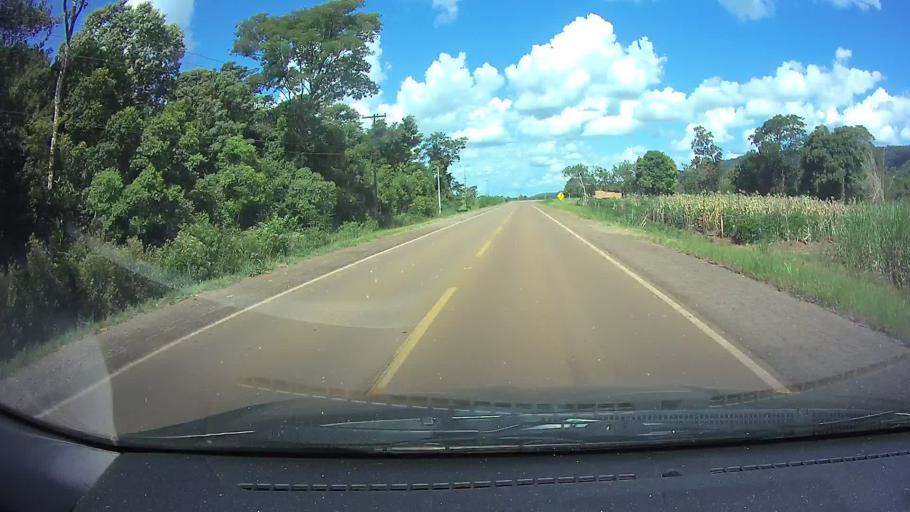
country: PY
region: Paraguari
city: La Colmena
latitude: -25.9062
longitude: -56.7650
